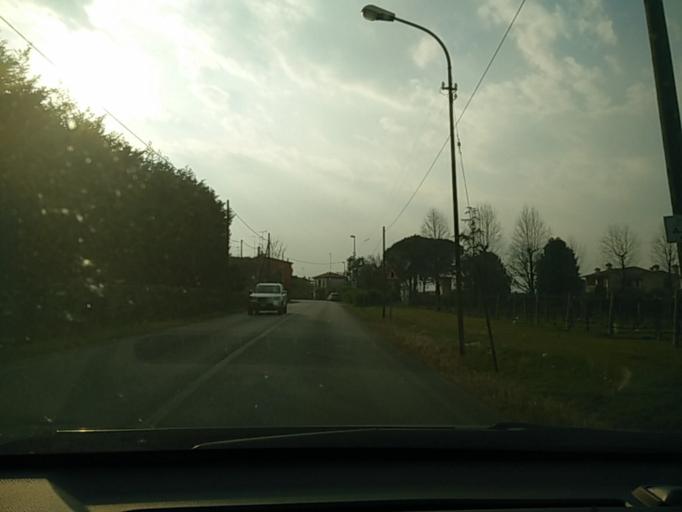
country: IT
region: Veneto
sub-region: Provincia di Treviso
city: San Michele di Piave
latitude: 45.8222
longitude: 12.3604
